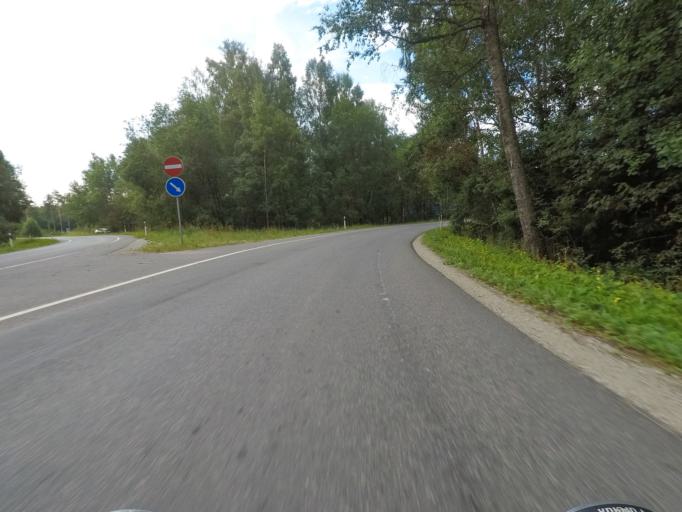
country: EE
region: Harju
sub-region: Saku vald
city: Saku
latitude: 59.3164
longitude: 24.6753
